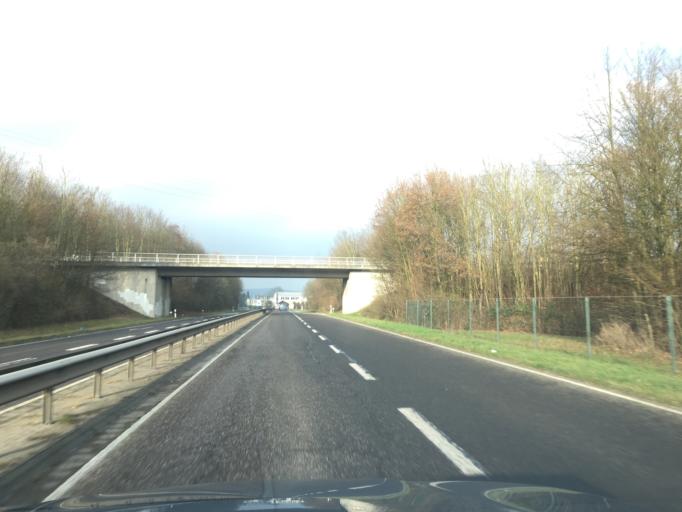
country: DE
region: Rheinland-Pfalz
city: Erpel
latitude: 50.5665
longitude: 7.2430
